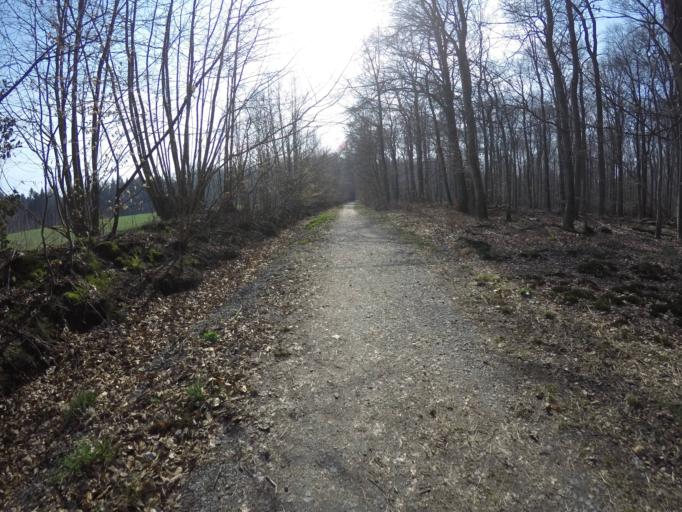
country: DE
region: Schleswig-Holstein
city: Borstel-Hohenraden
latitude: 53.7152
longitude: 9.8017
